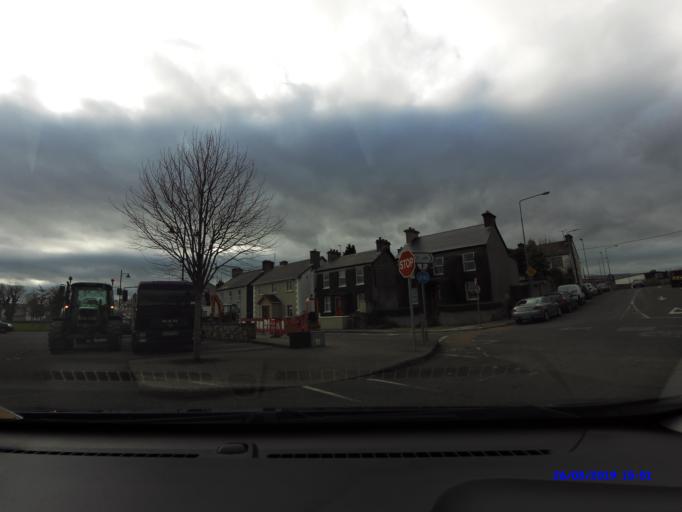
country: IE
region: Connaught
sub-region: Maigh Eo
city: Ballina
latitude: 54.1106
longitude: -9.1567
